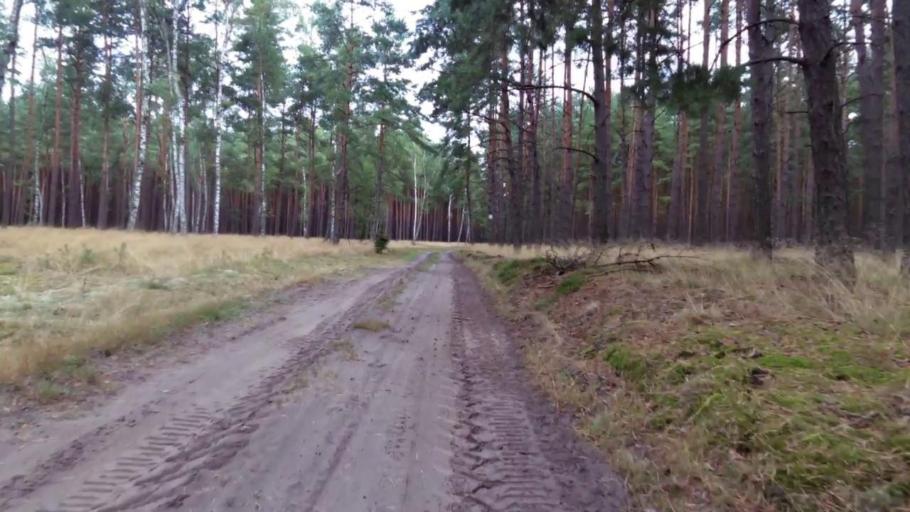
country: PL
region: West Pomeranian Voivodeship
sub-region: Powiat mysliborski
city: Debno
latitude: 52.8220
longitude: 14.6750
